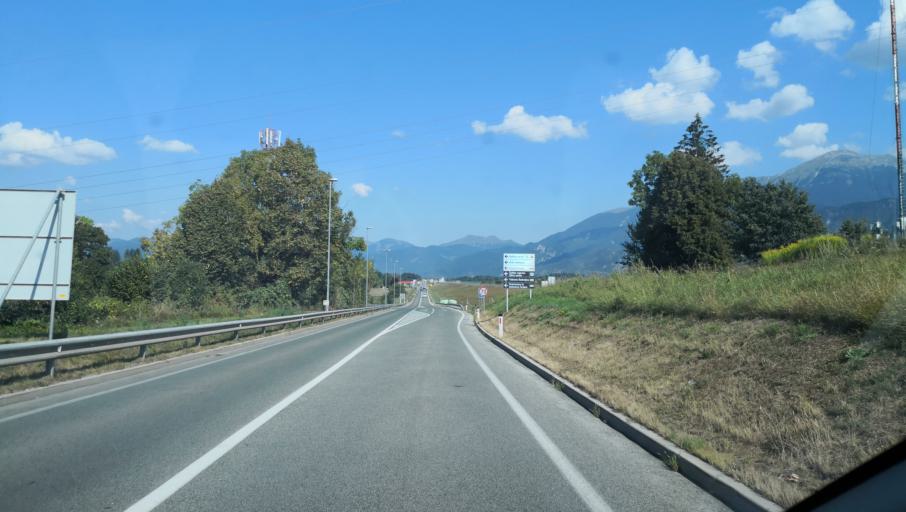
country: SI
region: Radovljica
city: Radovljica
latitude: 46.3418
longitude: 14.1864
